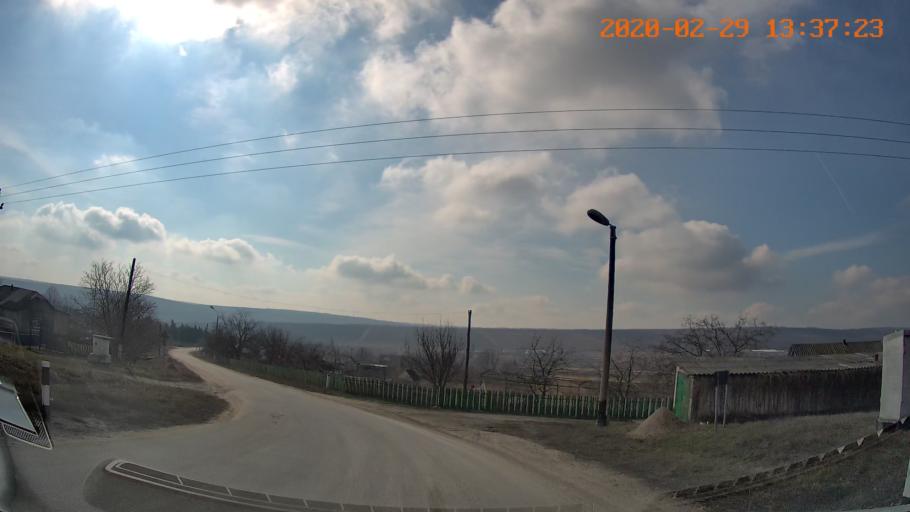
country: MD
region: Telenesti
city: Camenca
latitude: 47.8627
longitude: 28.6025
